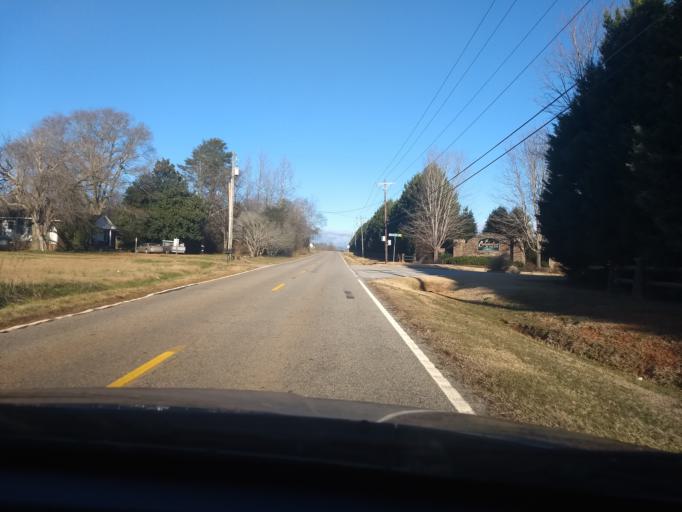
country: US
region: South Carolina
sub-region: Greenville County
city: Greer
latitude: 34.9812
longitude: -82.1970
